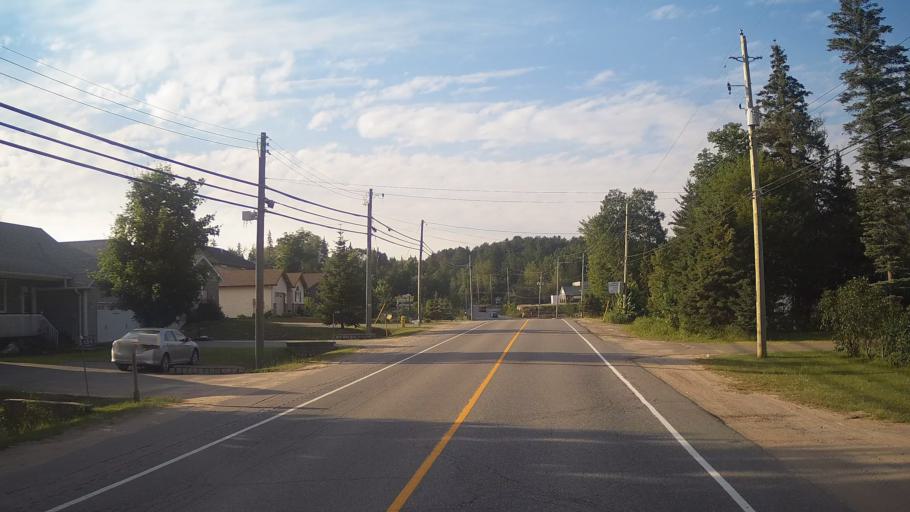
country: CA
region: Ontario
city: Huntsville
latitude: 45.3498
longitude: -79.2015
